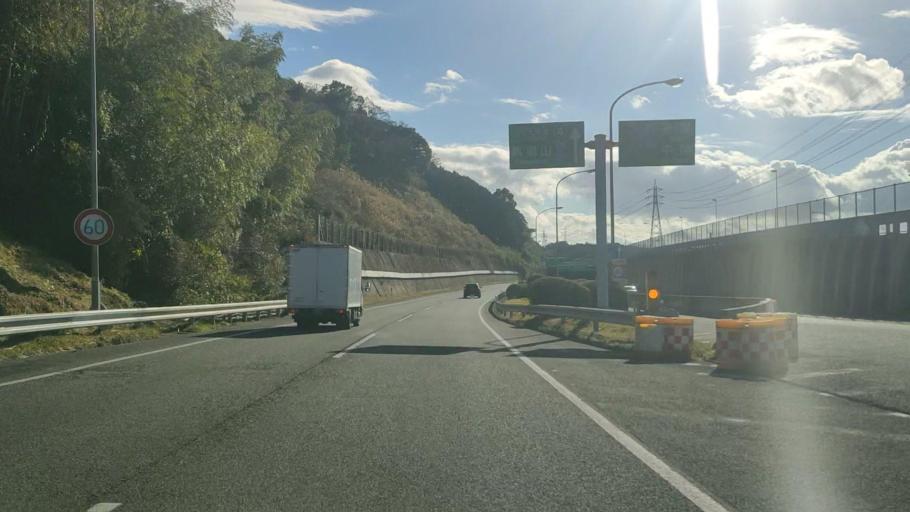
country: JP
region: Fukuoka
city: Kitakyushu
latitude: 33.8460
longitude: 130.7666
